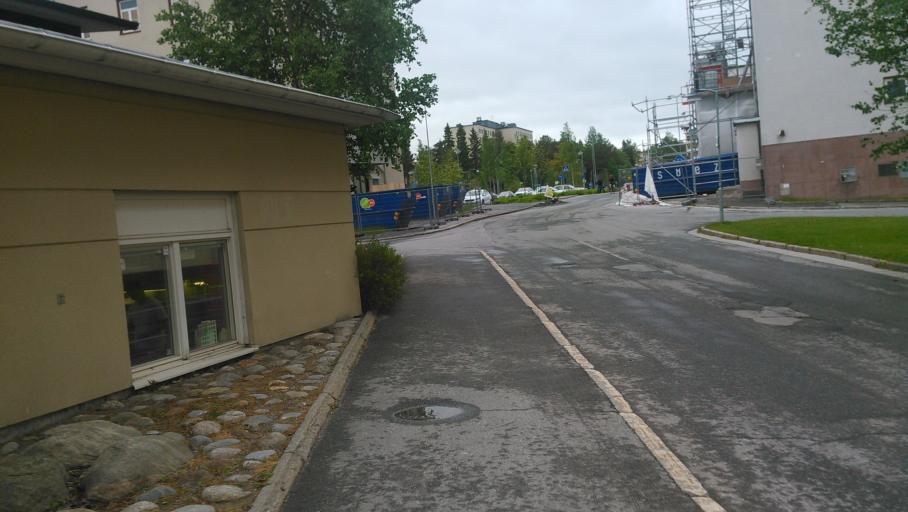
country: SE
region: Vaesterbotten
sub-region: Umea Kommun
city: Umea
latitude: 63.8168
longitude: 20.2974
